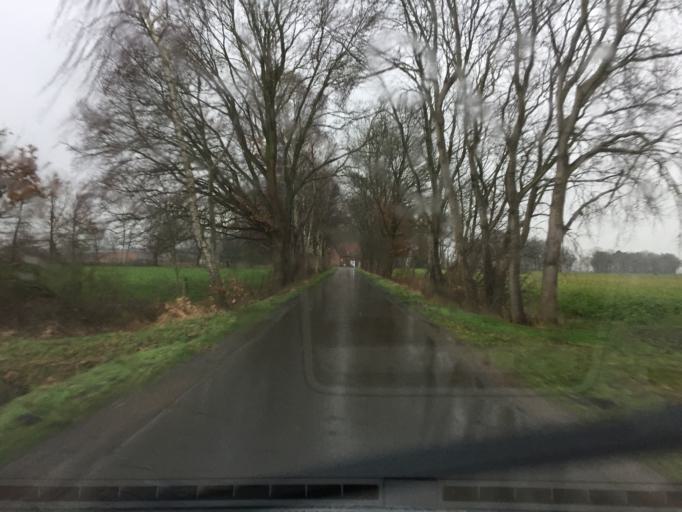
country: DE
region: Lower Saxony
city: Barenburg
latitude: 52.6468
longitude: 8.8331
